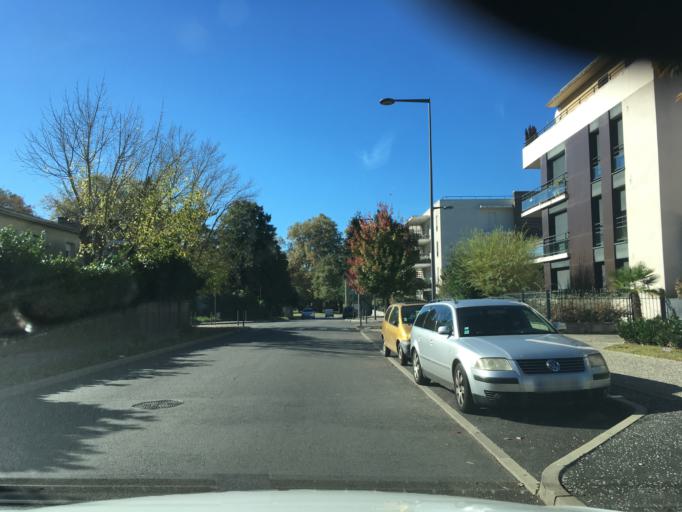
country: FR
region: Aquitaine
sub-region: Departement des Pyrenees-Atlantiques
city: Pau
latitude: 43.3153
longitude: -0.3488
